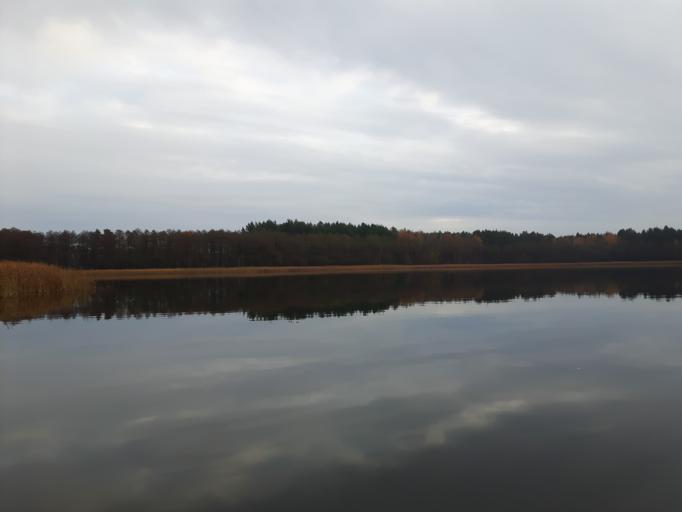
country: PL
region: Warmian-Masurian Voivodeship
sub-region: Powiat olsztynski
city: Barczewo
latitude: 53.8260
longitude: 20.7389
